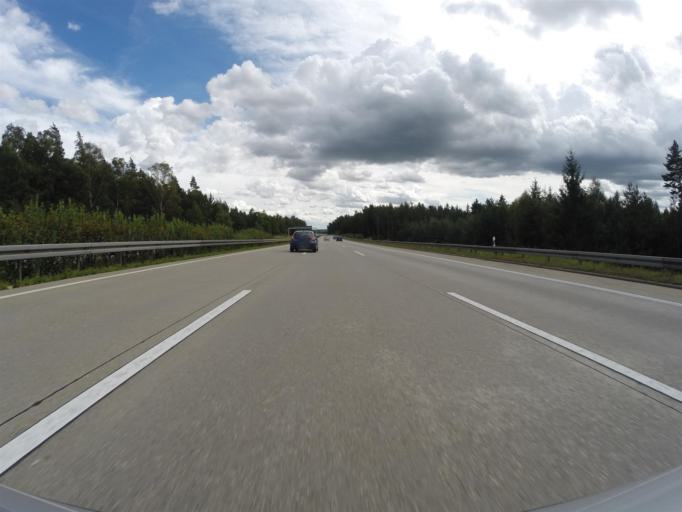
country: DE
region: Thuringia
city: Eineborn
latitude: 50.8482
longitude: 11.8605
